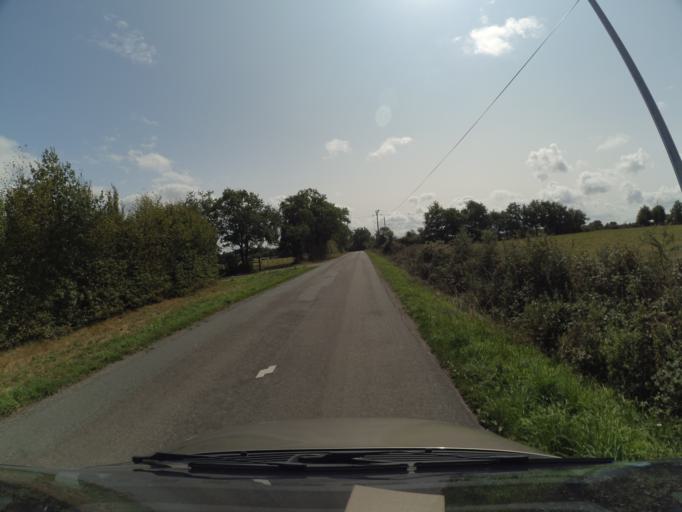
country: FR
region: Pays de la Loire
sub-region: Departement de la Vendee
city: La Bernardiere
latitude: 47.0309
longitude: -1.2360
